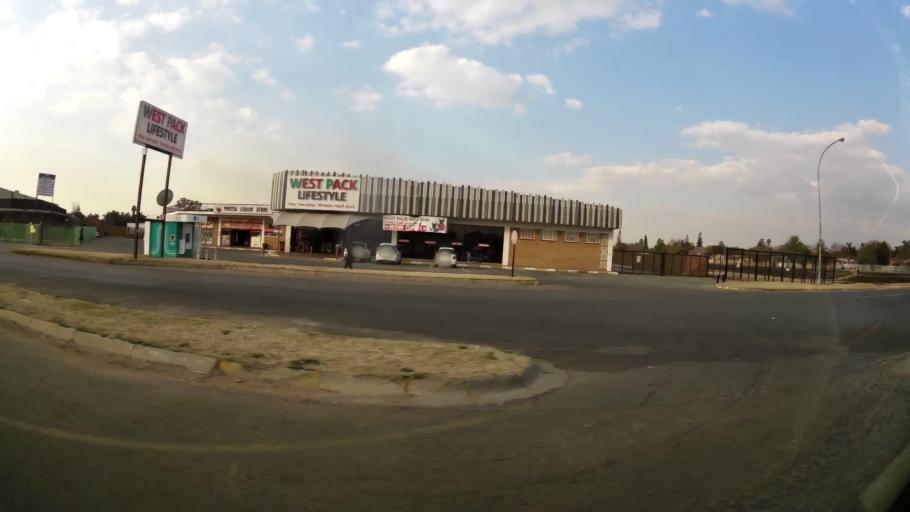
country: ZA
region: Gauteng
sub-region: Ekurhuleni Metropolitan Municipality
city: Benoni
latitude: -26.1458
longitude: 28.2985
